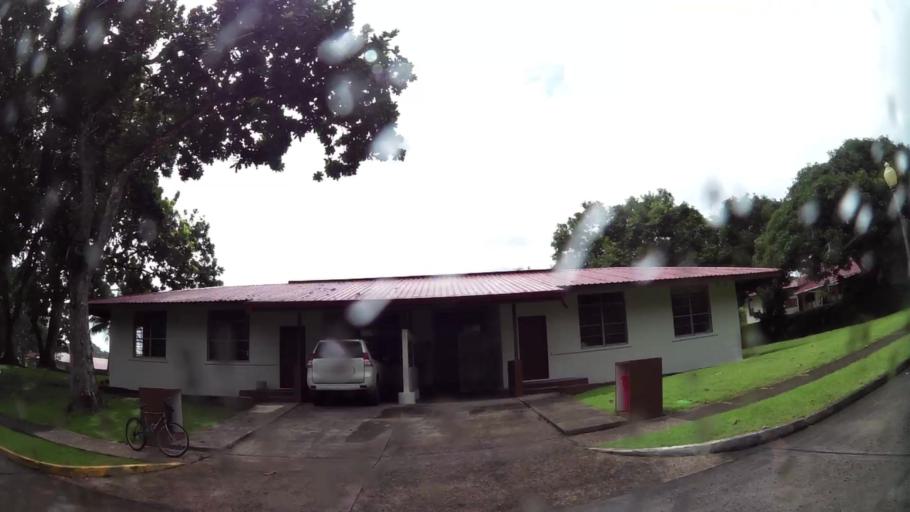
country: PA
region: Panama
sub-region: Distrito de Panama
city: Ancon
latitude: 9.0048
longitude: -79.5791
